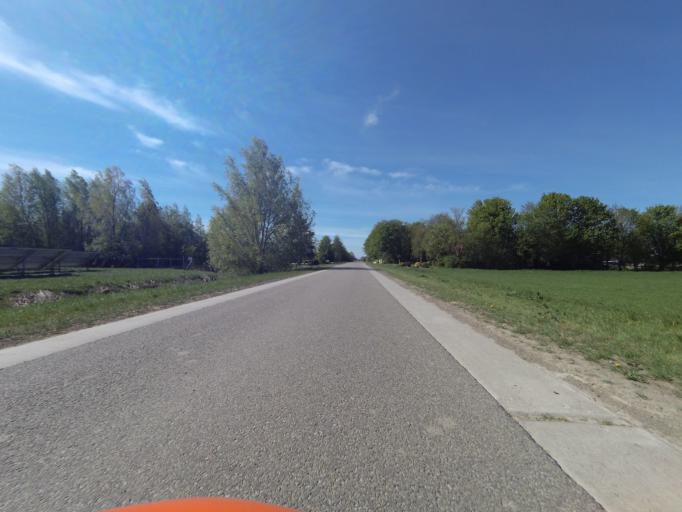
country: NL
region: Flevoland
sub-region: Gemeente Dronten
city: Biddinghuizen
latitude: 52.4269
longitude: 5.6860
